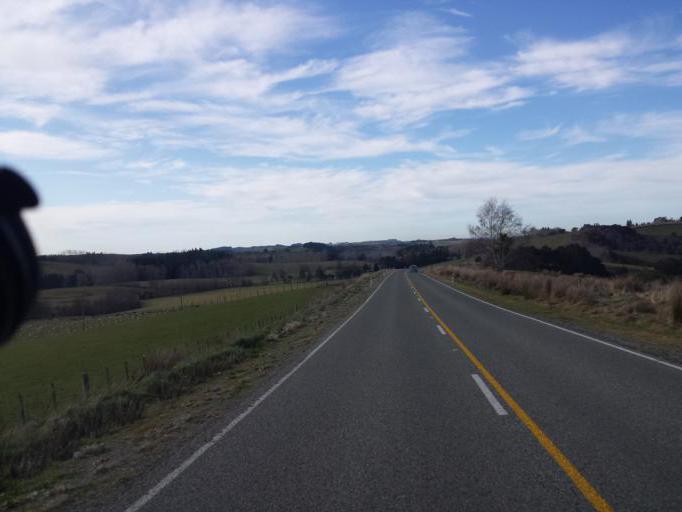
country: NZ
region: Canterbury
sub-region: Timaru District
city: Pleasant Point
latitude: -44.1206
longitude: 171.1151
